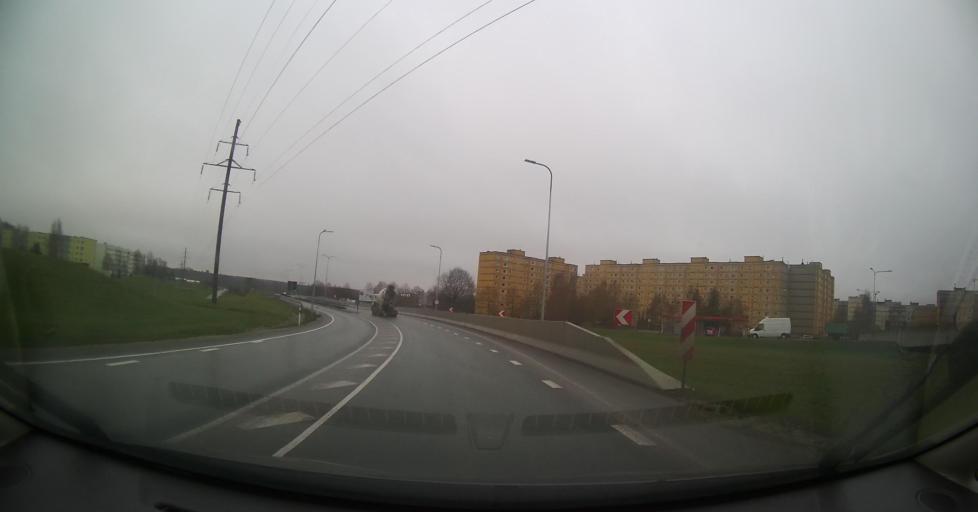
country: EE
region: Tartu
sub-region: Tartu linn
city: Tartu
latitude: 58.3758
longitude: 26.7821
